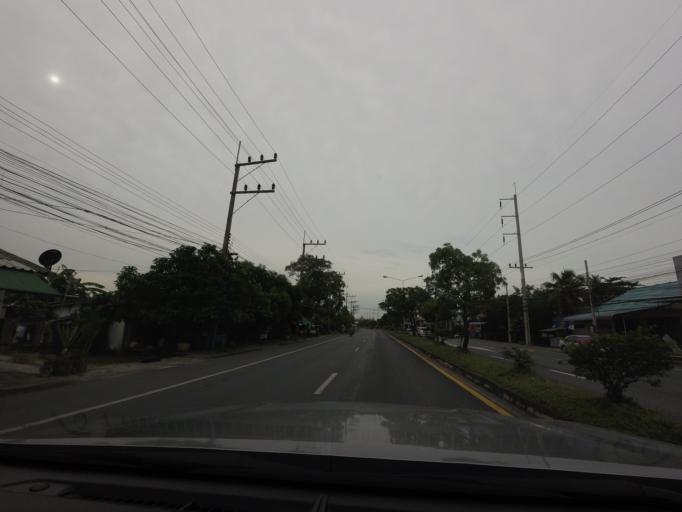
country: TH
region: Songkhla
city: Sathing Phra
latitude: 7.4754
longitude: 100.4391
